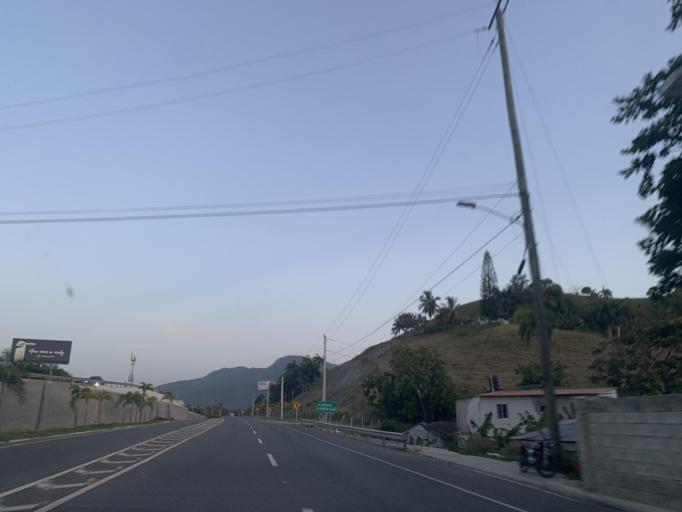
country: DO
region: Puerto Plata
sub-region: Puerto Plata
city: Puerto Plata
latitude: 19.8189
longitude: -70.7344
